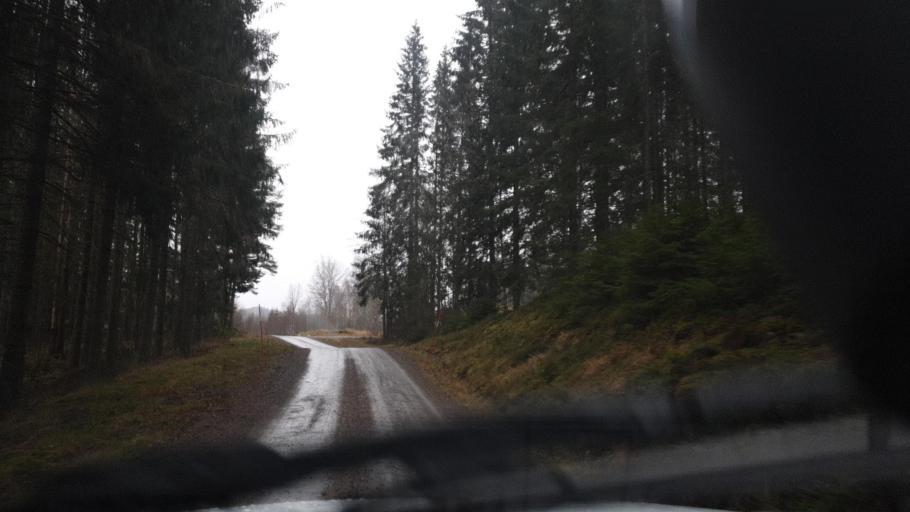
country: SE
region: Vaermland
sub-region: Eda Kommun
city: Amotfors
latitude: 59.8095
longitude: 12.4160
